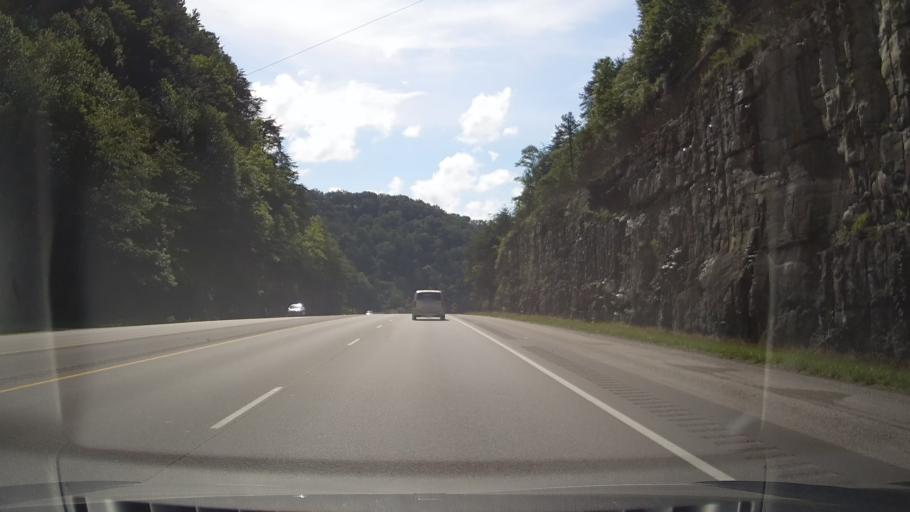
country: US
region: Kentucky
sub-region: Floyd County
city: Prestonsburg
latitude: 37.6440
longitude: -82.7720
